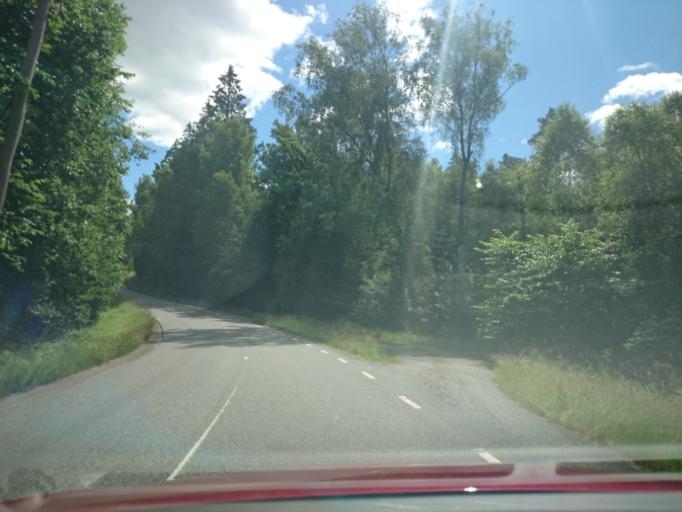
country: SE
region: Vaestra Goetaland
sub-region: Lerums Kommun
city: Lerum
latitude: 57.8051
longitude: 12.1955
